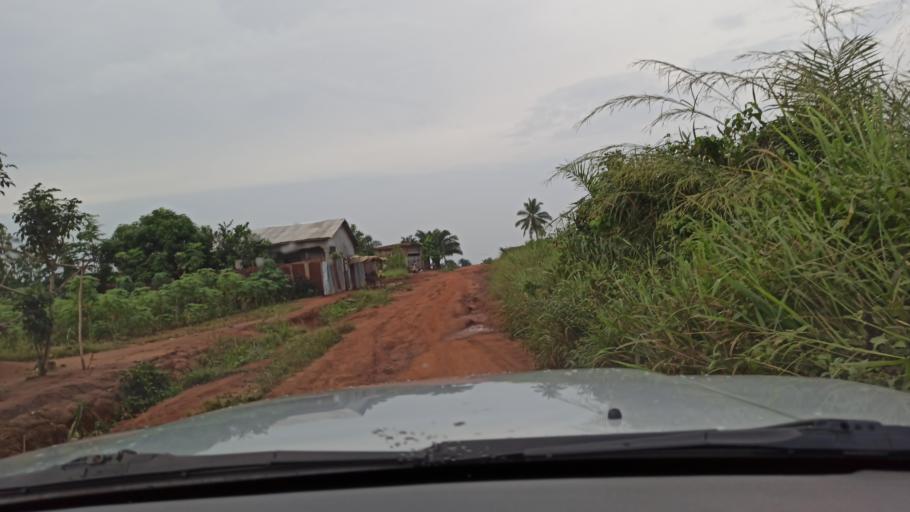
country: BJ
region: Queme
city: Porto-Novo
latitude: 6.4672
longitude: 2.6721
